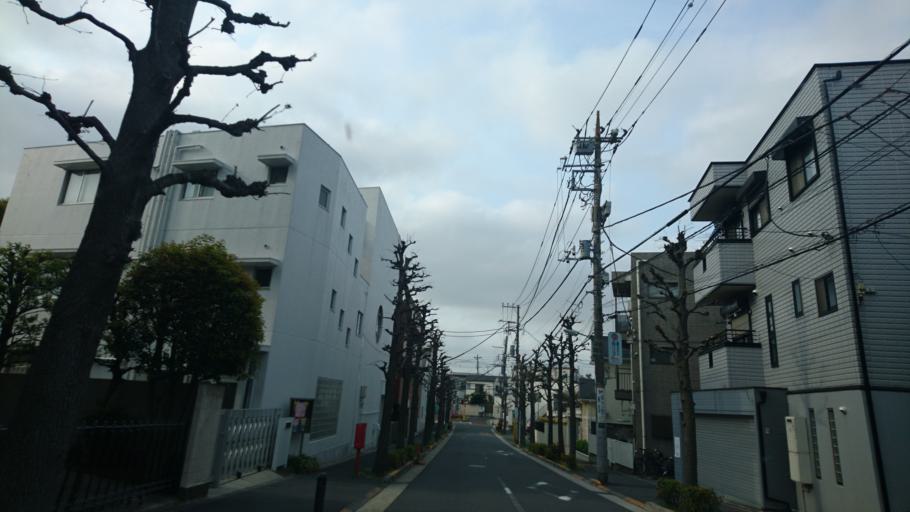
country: JP
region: Kanagawa
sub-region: Kawasaki-shi
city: Kawasaki
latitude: 35.5976
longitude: 139.7251
